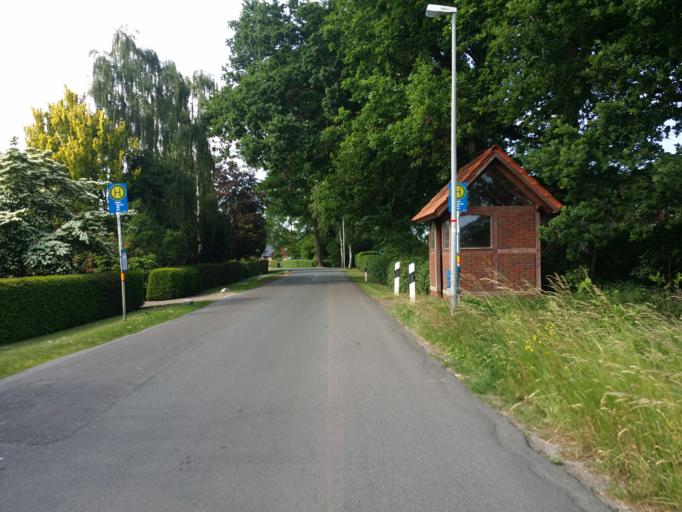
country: DE
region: Lower Saxony
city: Bockhorn
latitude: 53.3392
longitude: 8.0312
